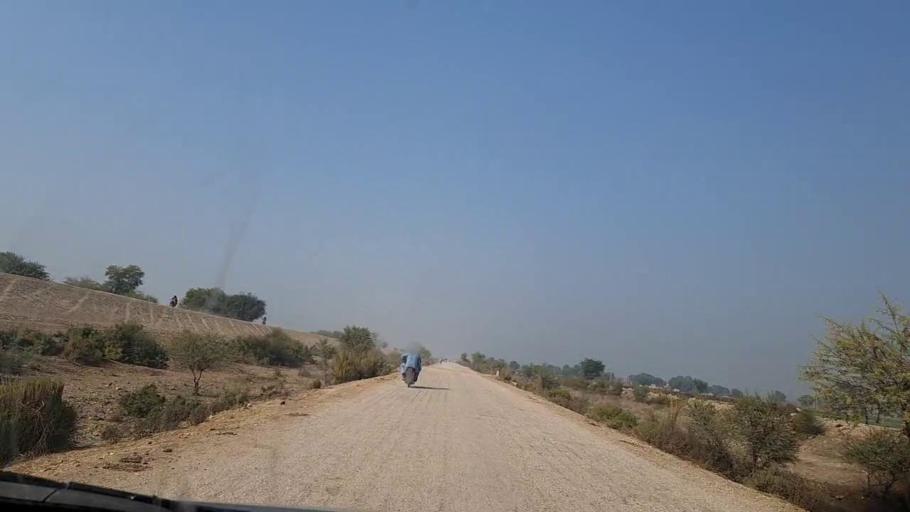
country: PK
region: Sindh
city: Moro
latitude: 26.7160
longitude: 67.9238
